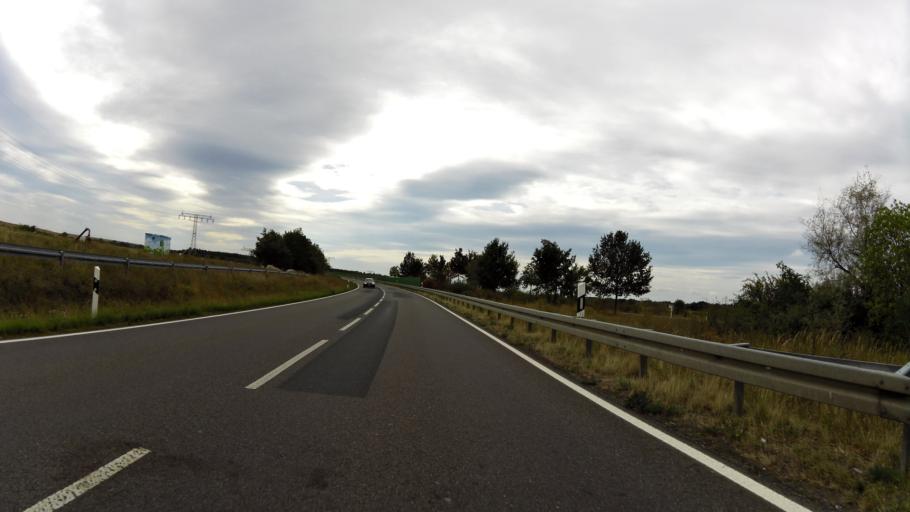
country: DE
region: Brandenburg
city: Heinersbruck
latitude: 51.8127
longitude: 14.5069
